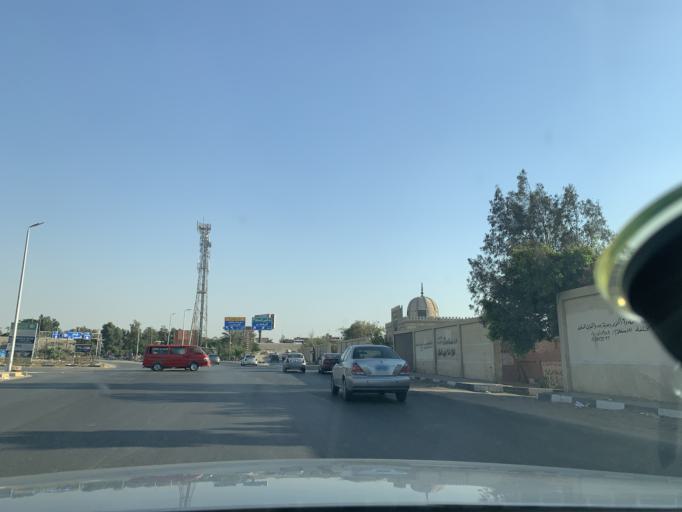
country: EG
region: Muhafazat al Qahirah
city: Cairo
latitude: 30.0256
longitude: 31.3537
